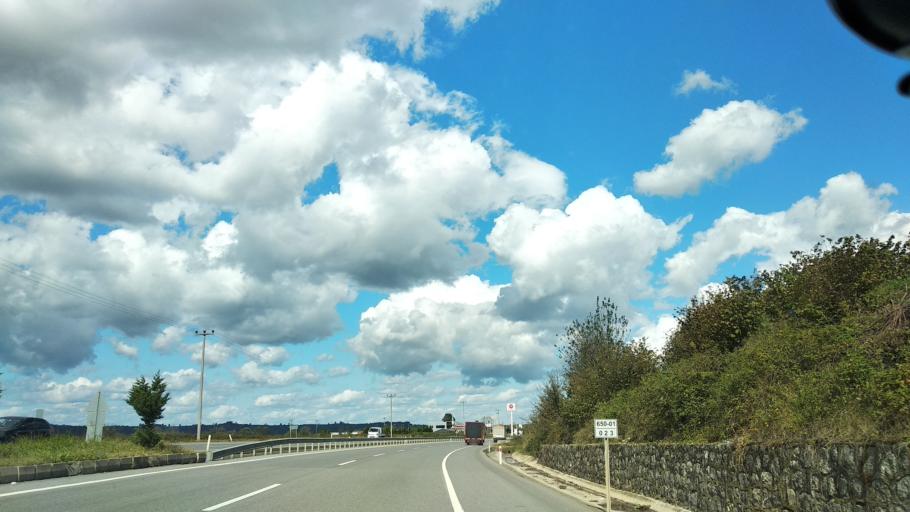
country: TR
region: Sakarya
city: Ferizli
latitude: 40.9705
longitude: 30.5082
